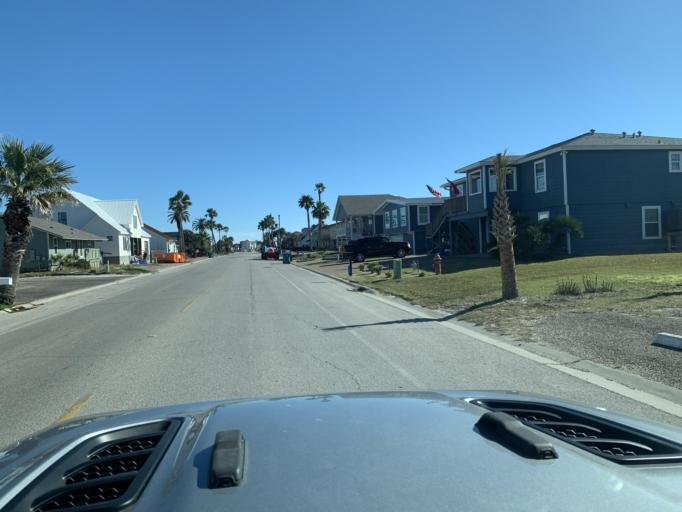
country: US
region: Texas
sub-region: Aransas County
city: Fulton
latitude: 28.0461
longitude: -97.0285
